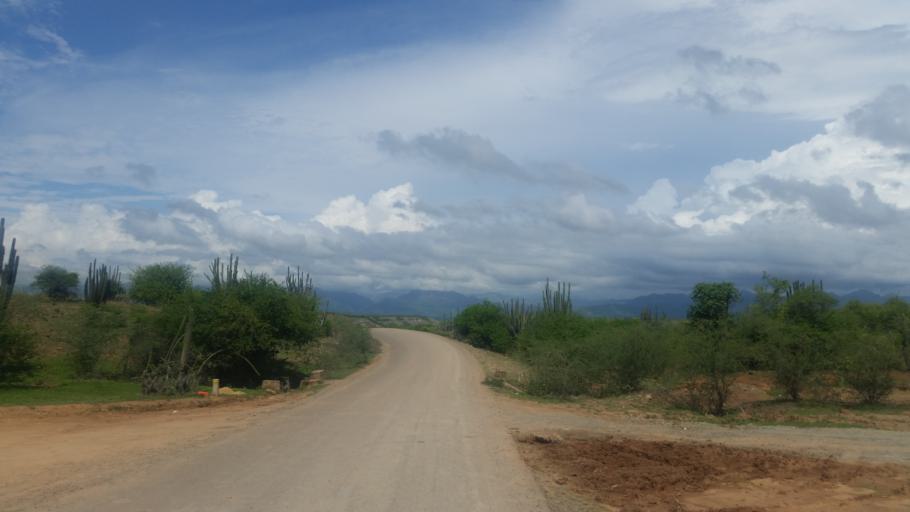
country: CO
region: Huila
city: Villavieja
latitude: 3.2338
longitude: -75.1712
